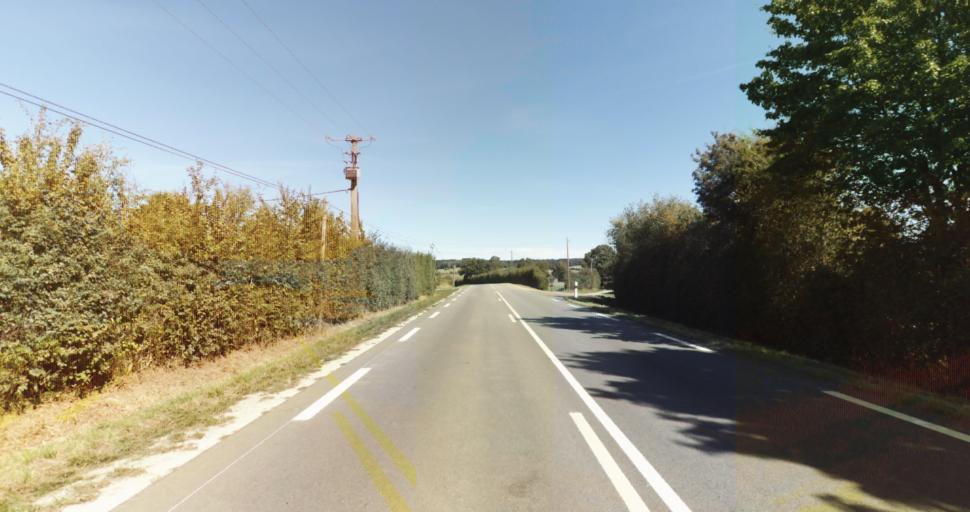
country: FR
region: Lower Normandy
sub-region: Departement de l'Orne
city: Gace
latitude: 48.7691
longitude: 0.2912
